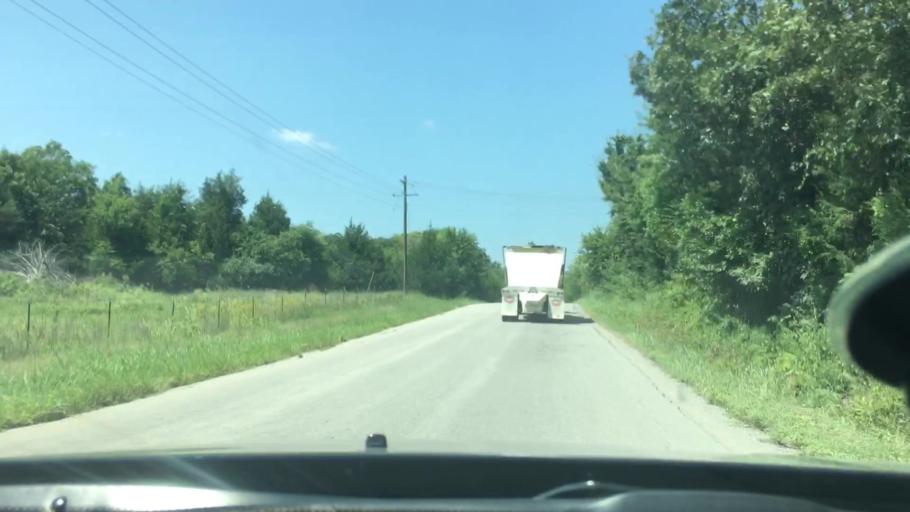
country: US
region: Oklahoma
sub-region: Bryan County
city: Durant
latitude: 34.2587
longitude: -96.3852
